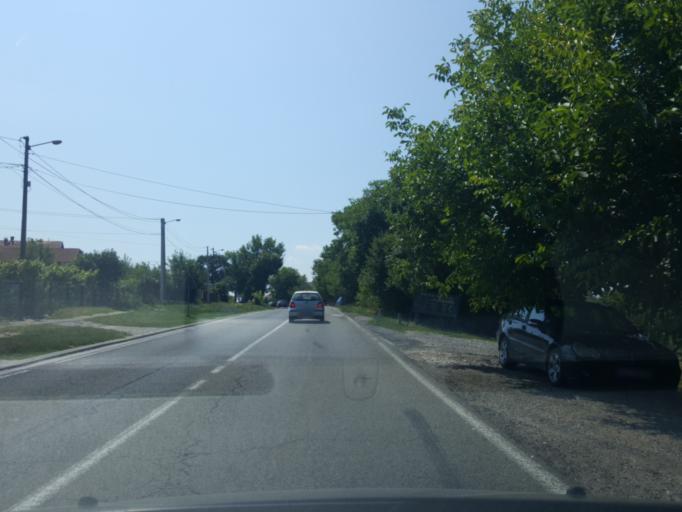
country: RS
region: Central Serbia
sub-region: Belgrade
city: Mladenovac
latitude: 44.4568
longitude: 20.6763
